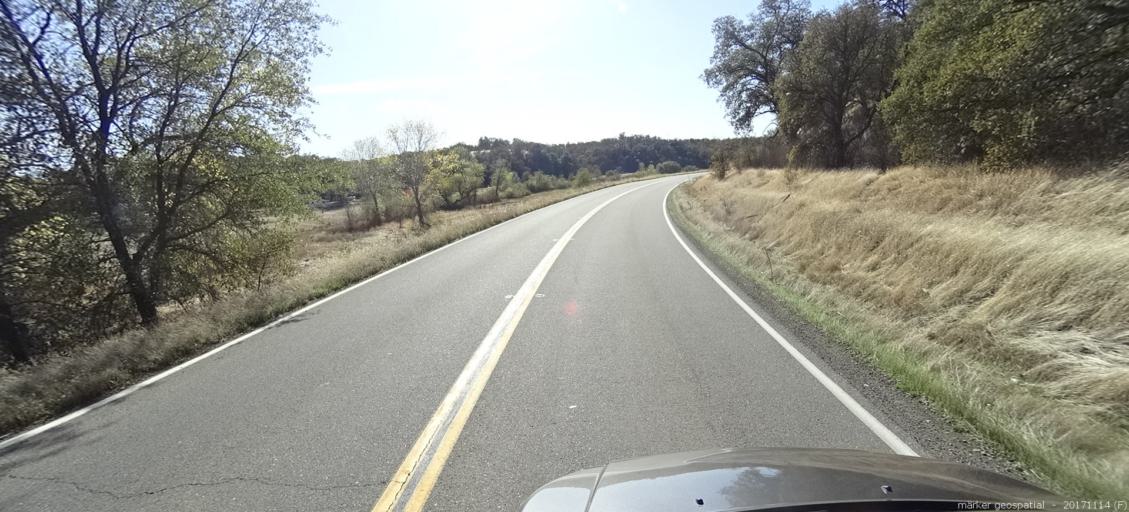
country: US
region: California
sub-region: Shasta County
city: Anderson
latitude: 40.4385
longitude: -122.3041
